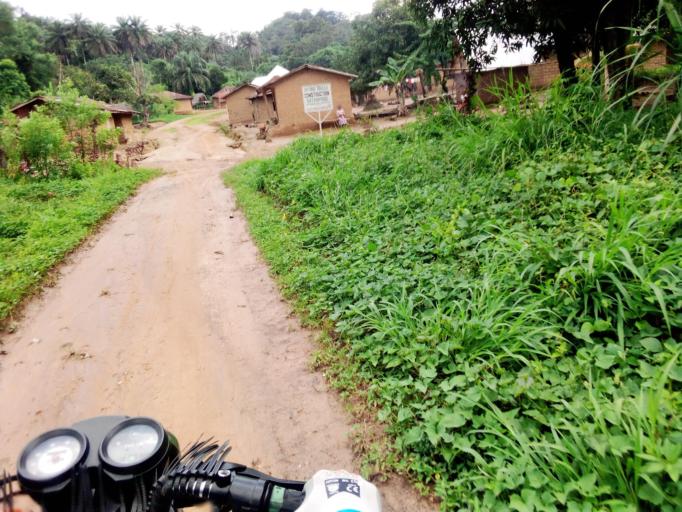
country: SL
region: Eastern Province
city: Giehun
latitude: 8.5635
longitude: -10.9963
